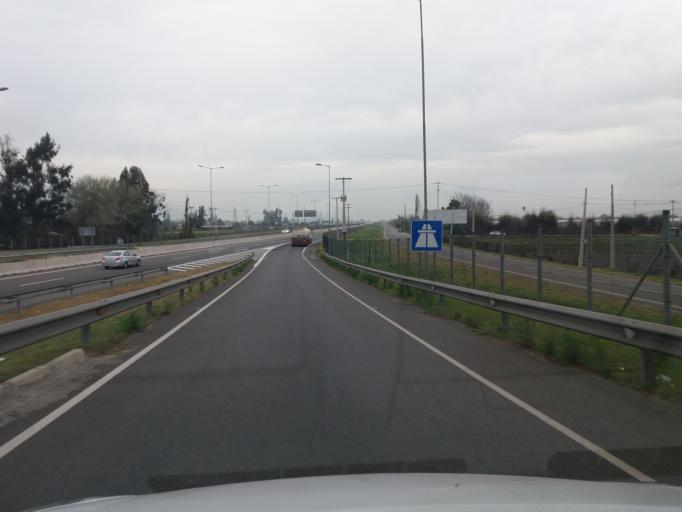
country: CL
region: Valparaiso
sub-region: Provincia de Quillota
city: Quillota
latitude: -32.9263
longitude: -71.2828
